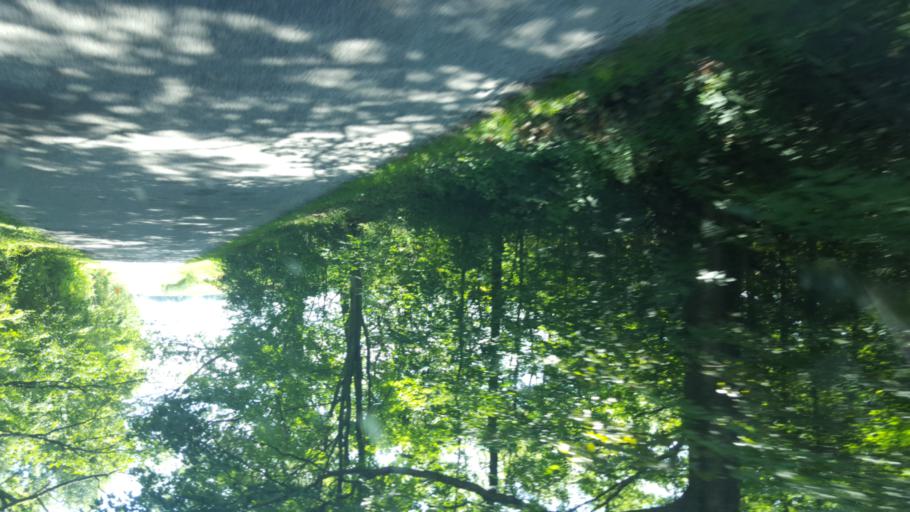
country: US
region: Ohio
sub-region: Knox County
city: Centerburg
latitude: 40.4034
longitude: -82.7402
